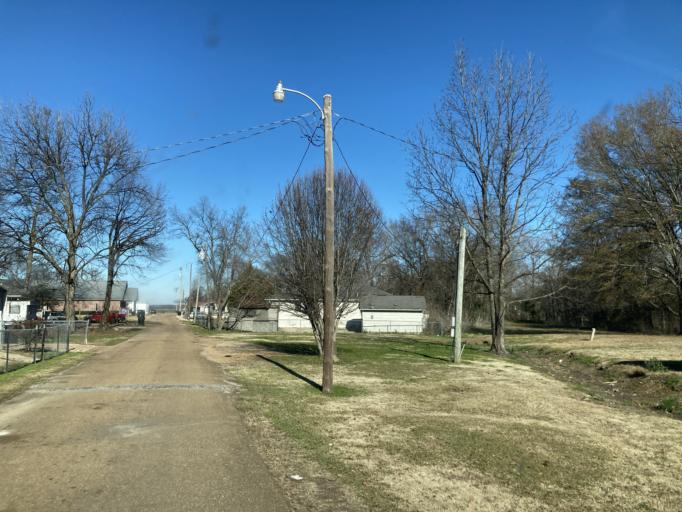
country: US
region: Mississippi
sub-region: Yazoo County
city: Yazoo City
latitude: 32.9783
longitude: -90.5934
